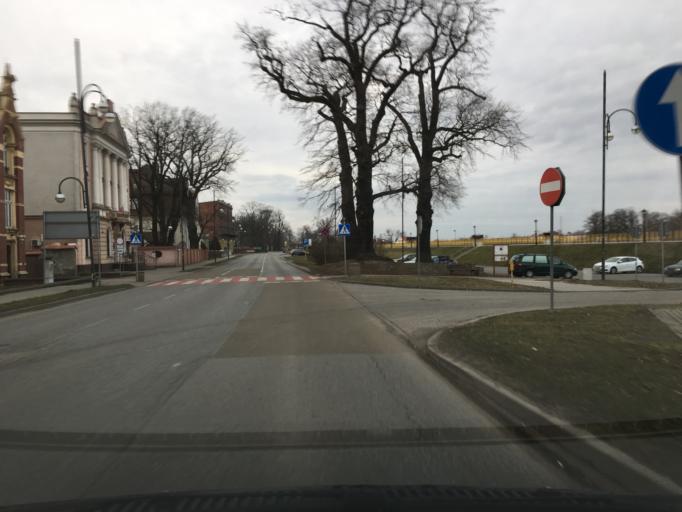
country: PL
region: Opole Voivodeship
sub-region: Powiat kedzierzynsko-kozielski
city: Kozle
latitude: 50.3358
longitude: 18.1470
